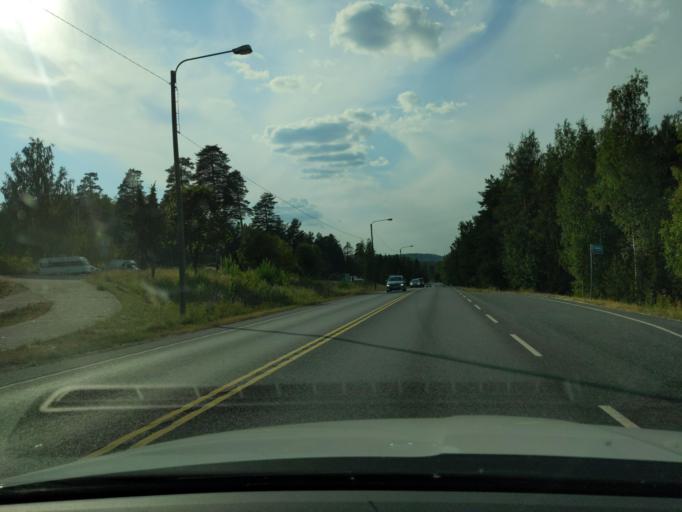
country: FI
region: Paijanne Tavastia
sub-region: Lahti
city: Asikkala
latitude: 61.1658
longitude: 25.5653
